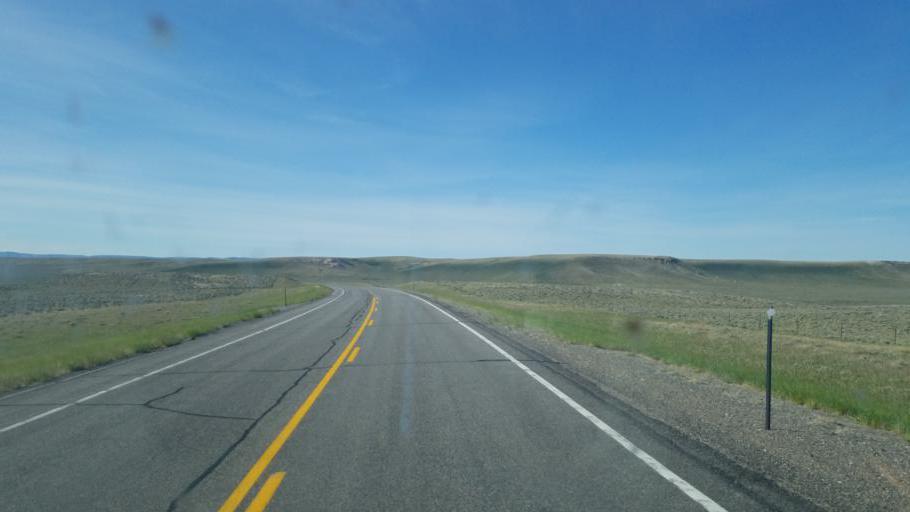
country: US
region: Wyoming
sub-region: Fremont County
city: Riverton
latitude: 42.6255
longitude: -108.1964
